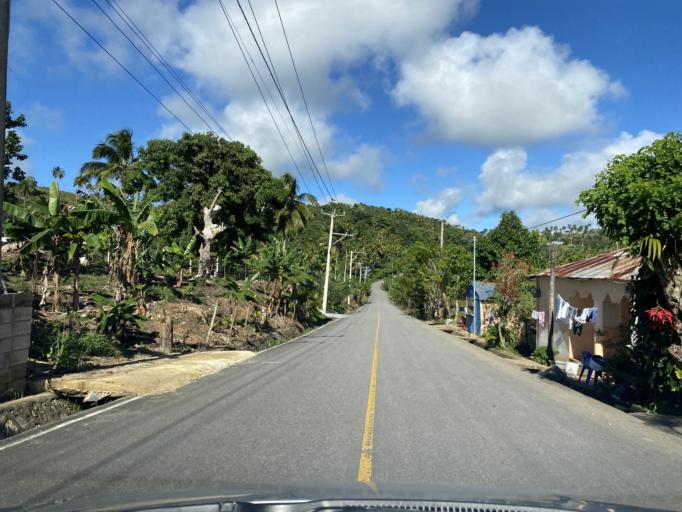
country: DO
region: Samana
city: Sanchez
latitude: 19.2536
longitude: -69.5813
